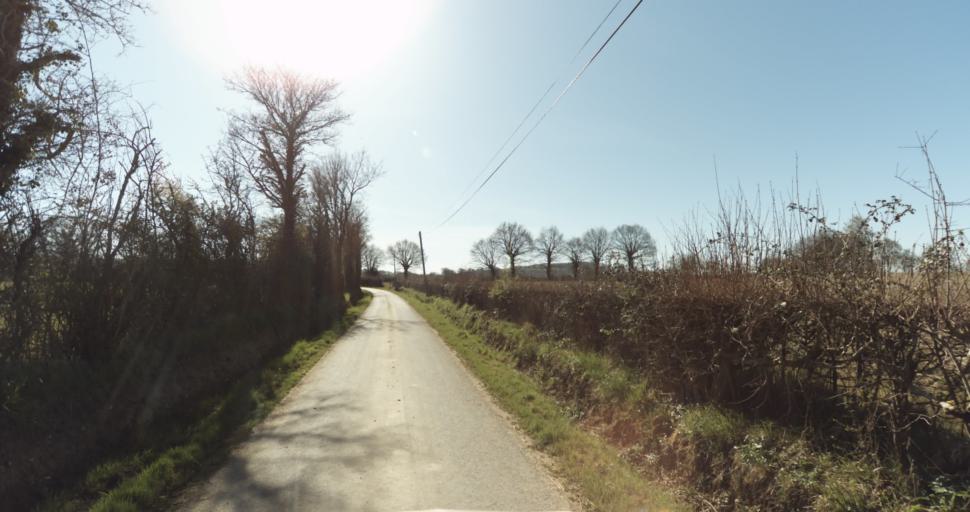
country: FR
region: Lower Normandy
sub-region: Departement de l'Orne
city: Trun
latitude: 48.9170
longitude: 0.0388
